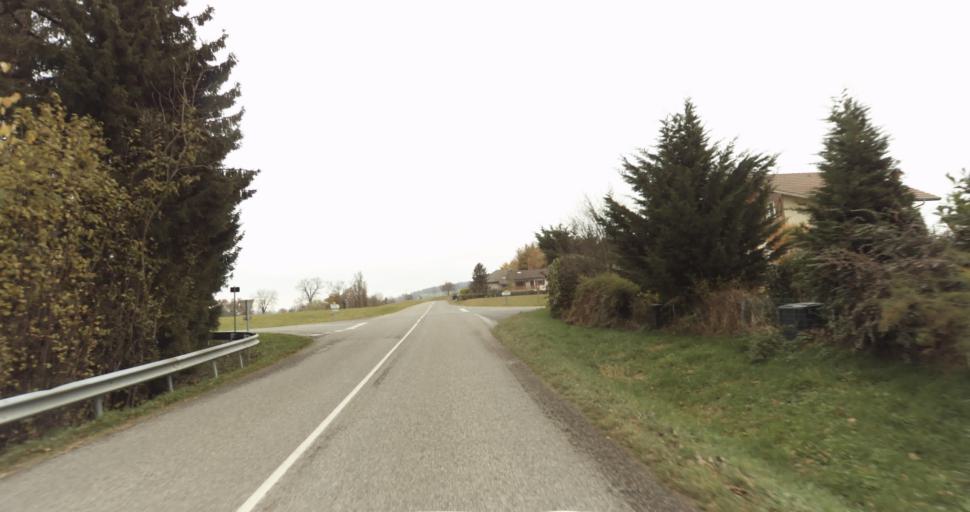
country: FR
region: Rhone-Alpes
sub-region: Departement de la Haute-Savoie
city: Viuz-la-Chiesaz
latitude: 45.8380
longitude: 6.0435
